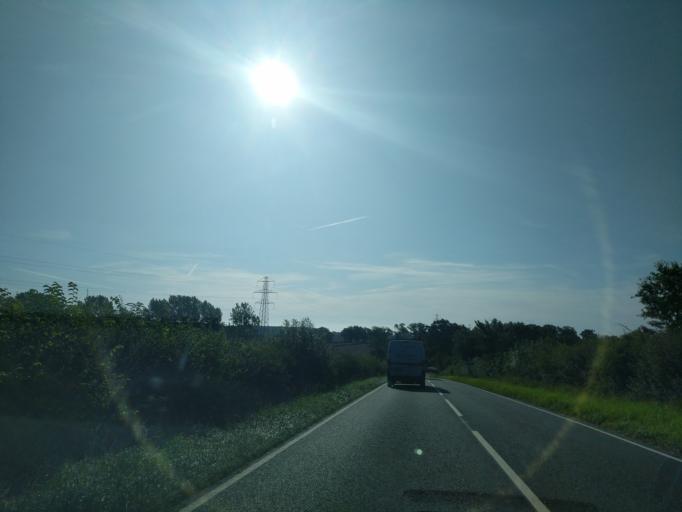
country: GB
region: England
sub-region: Lincolnshire
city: Bourne
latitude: 52.8016
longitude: -0.4546
